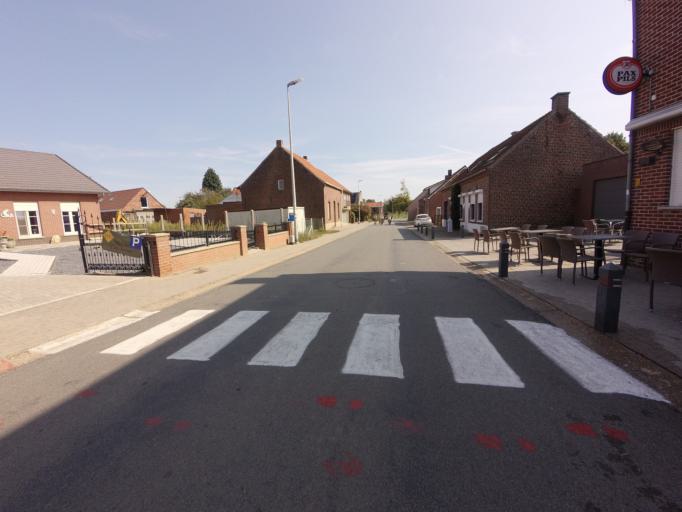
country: NL
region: Limburg
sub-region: Gemeente Maasgouw
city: Maasbracht
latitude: 51.1524
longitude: 5.8244
